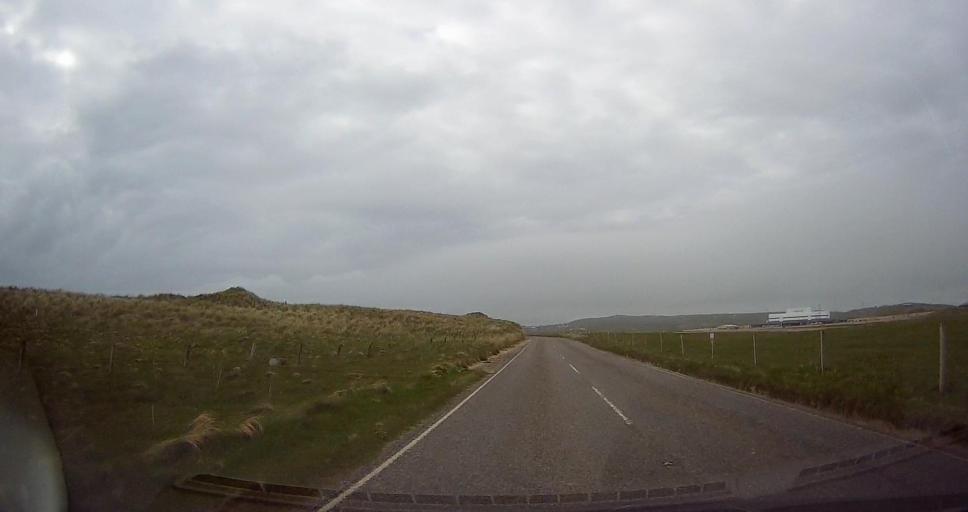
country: GB
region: Scotland
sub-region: Shetland Islands
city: Sandwick
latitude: 59.8718
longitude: -1.2875
